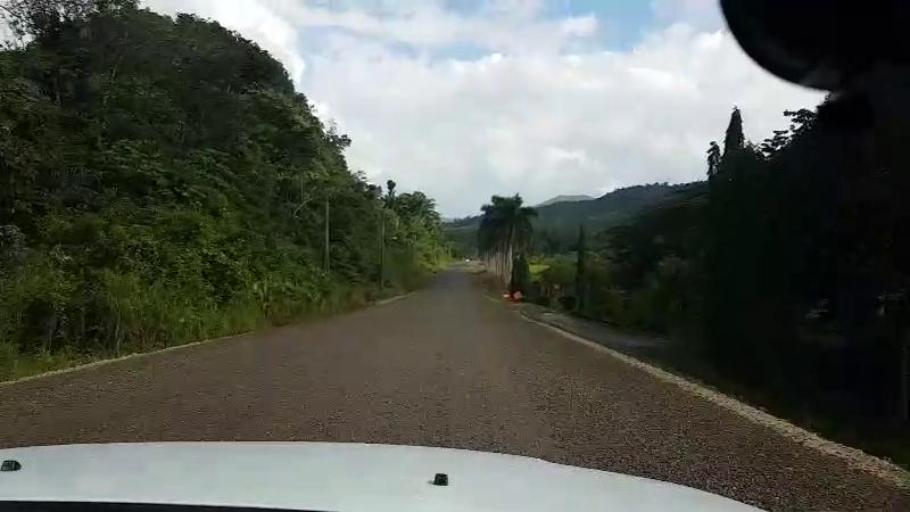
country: BZ
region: Cayo
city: Belmopan
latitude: 17.0912
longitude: -88.6245
